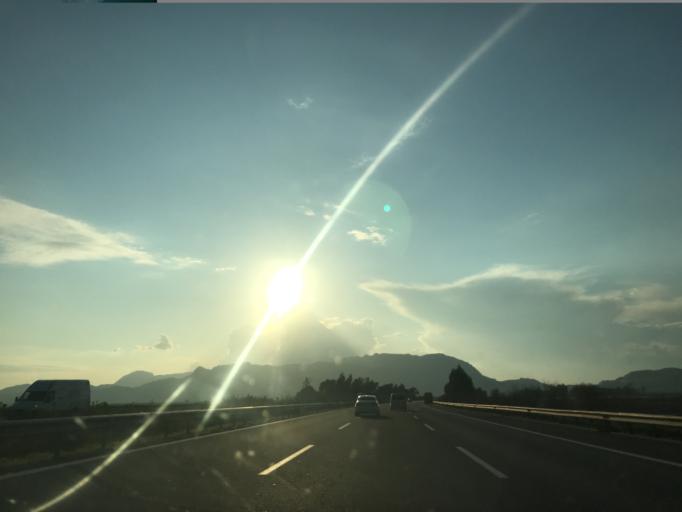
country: TR
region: Adana
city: Ceyhan
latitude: 36.9827
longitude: 35.7911
